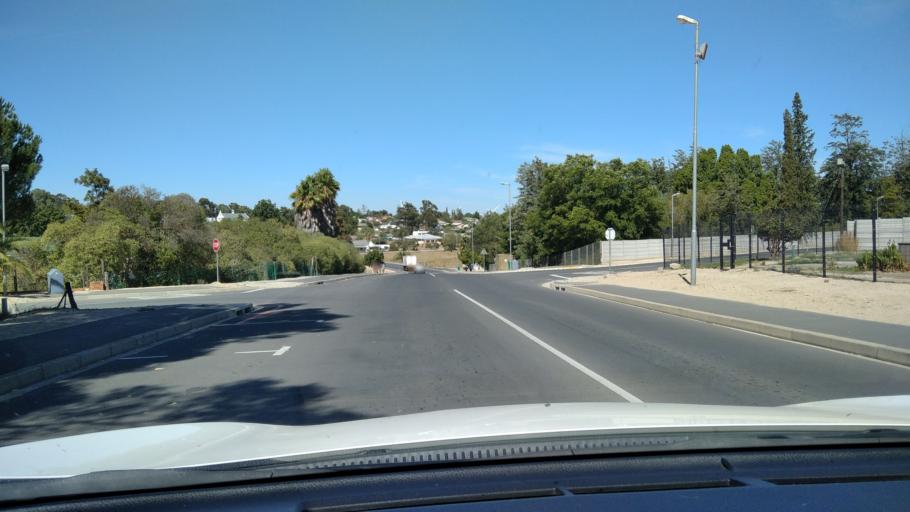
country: ZA
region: Western Cape
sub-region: West Coast District Municipality
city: Moorreesburg
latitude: -33.0605
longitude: 18.3426
